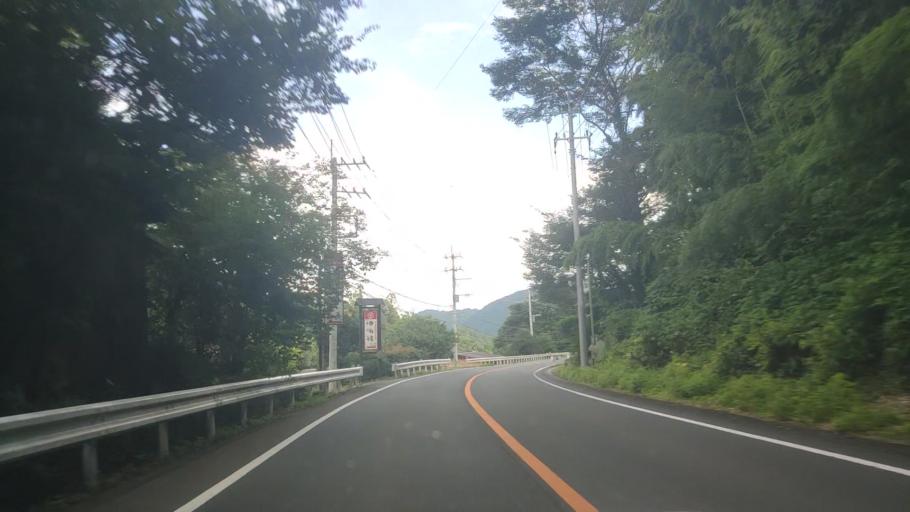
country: JP
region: Gunma
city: Omamacho-omama
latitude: 36.4738
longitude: 139.2578
